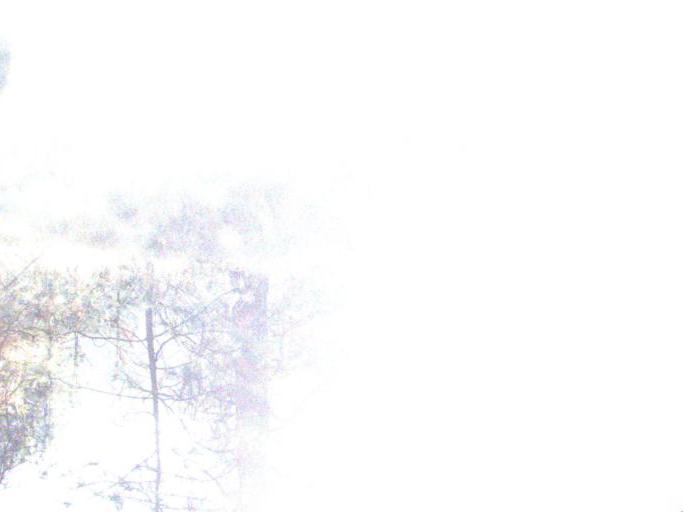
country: CA
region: British Columbia
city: Rossland
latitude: 48.8843
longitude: -117.8316
